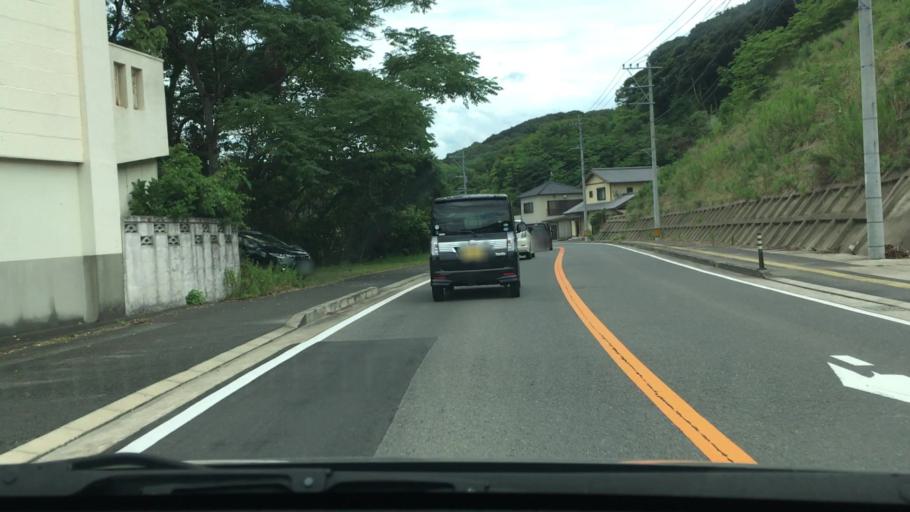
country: JP
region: Nagasaki
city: Togitsu
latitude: 32.9869
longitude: 129.7751
